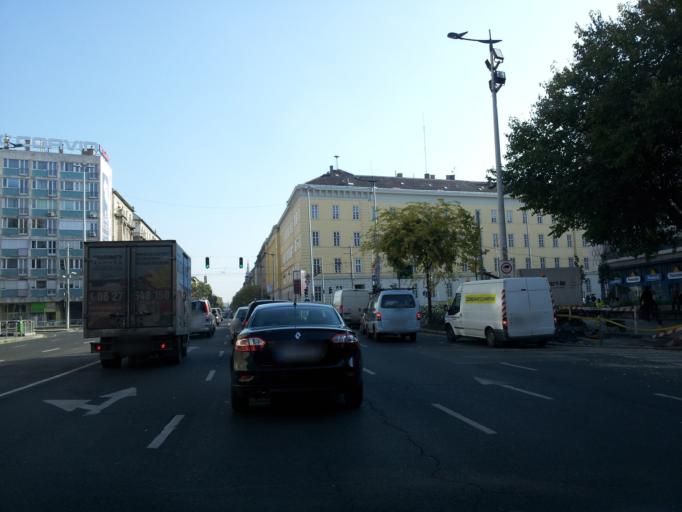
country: HU
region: Budapest
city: Budapest VIII. keruelet
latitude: 47.4861
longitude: 19.0691
